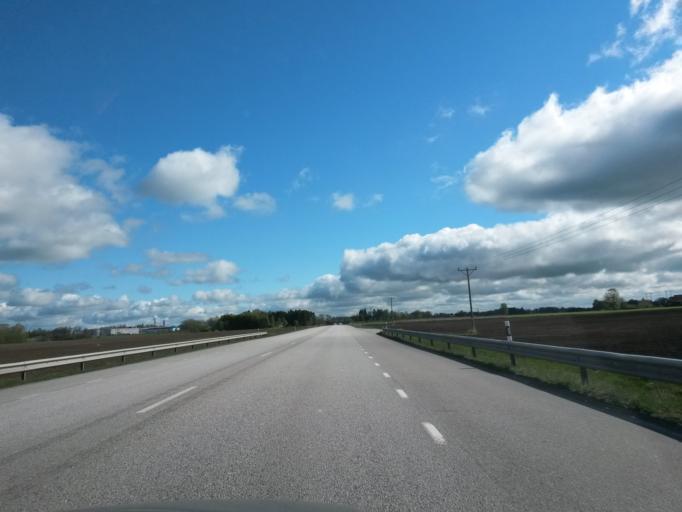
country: SE
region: Vaestra Goetaland
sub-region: Vara Kommun
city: Vara
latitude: 58.2476
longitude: 12.9517
